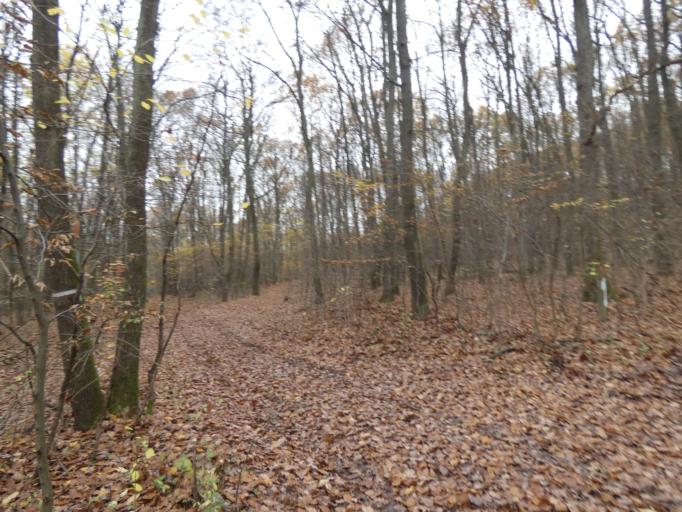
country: HU
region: Pest
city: Kismaros
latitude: 47.8870
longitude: 18.9416
